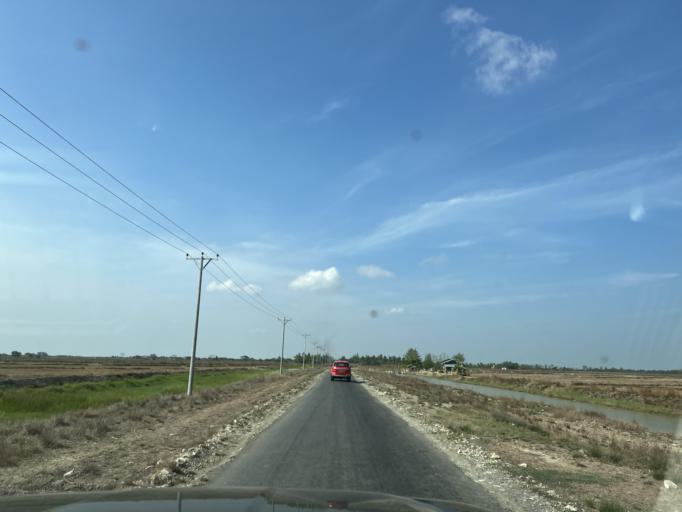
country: MM
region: Ayeyarwady
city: Pyapon
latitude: 16.0259
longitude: 95.6079
